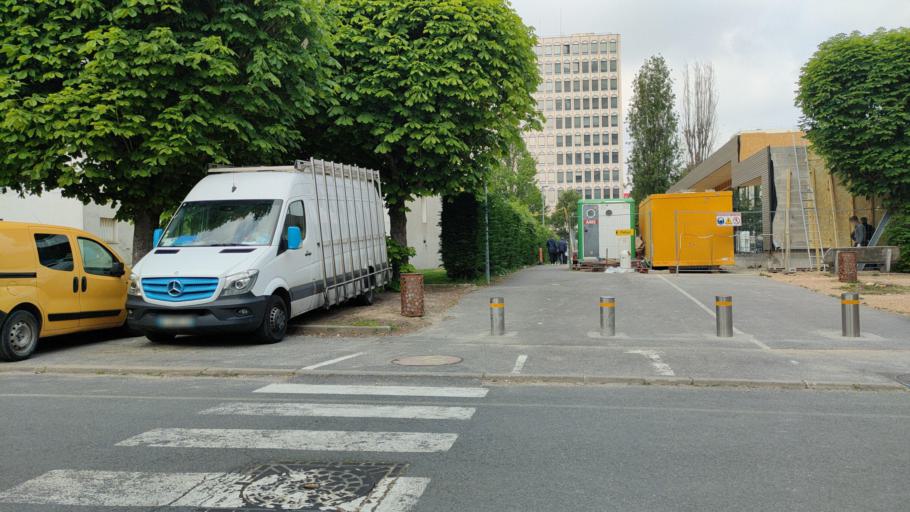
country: FR
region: Ile-de-France
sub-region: Departement du Val-de-Marne
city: Maisons-Alfort
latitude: 48.7962
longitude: 2.4517
